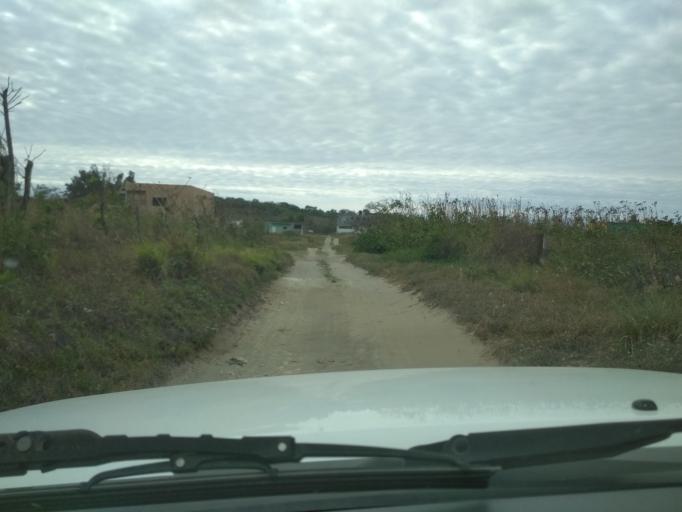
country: MX
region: Veracruz
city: Anton Lizardo
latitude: 19.0524
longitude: -95.9880
